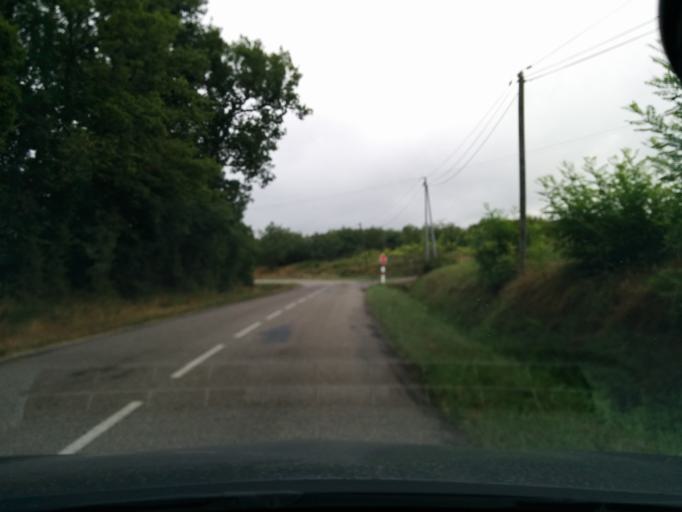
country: FR
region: Midi-Pyrenees
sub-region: Departement du Tarn-et-Garonne
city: Moissac
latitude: 44.1529
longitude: 1.0652
